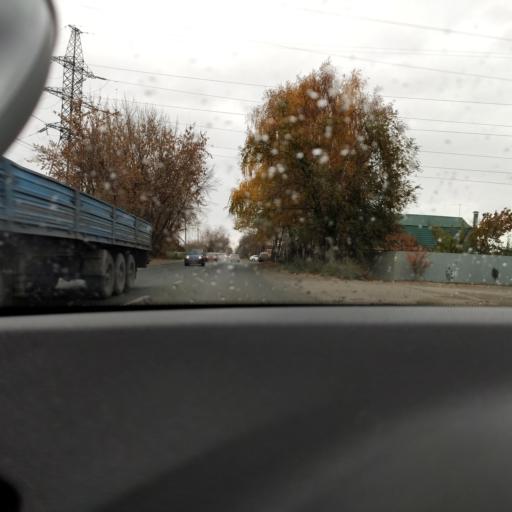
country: RU
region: Samara
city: Smyshlyayevka
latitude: 53.2354
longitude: 50.3155
